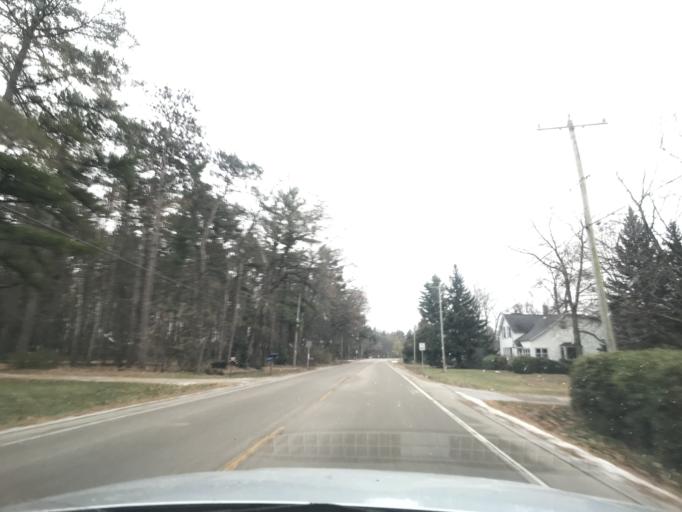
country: US
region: Wisconsin
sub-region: Marinette County
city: Marinette
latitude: 45.0649
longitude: -87.6193
